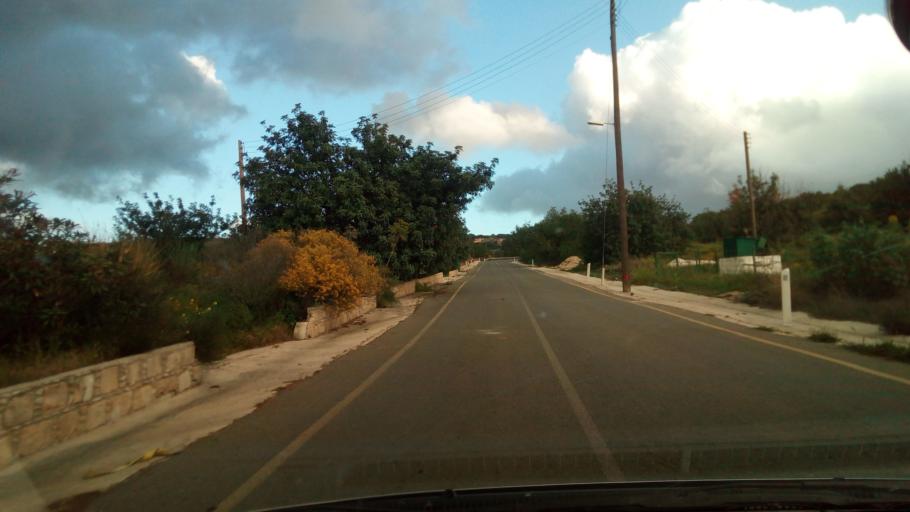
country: CY
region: Pafos
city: Polis
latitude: 34.9891
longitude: 32.4927
